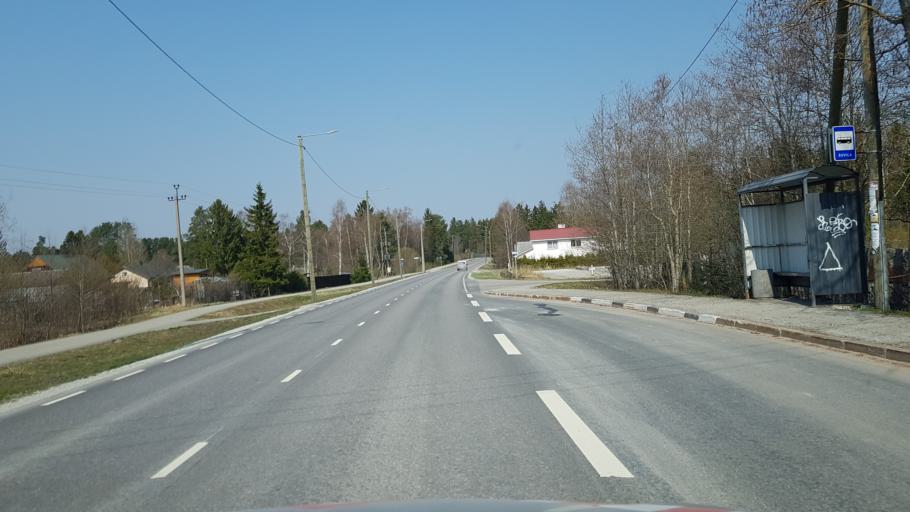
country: EE
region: Harju
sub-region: Saku vald
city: Saku
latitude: 59.2094
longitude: 24.6630
